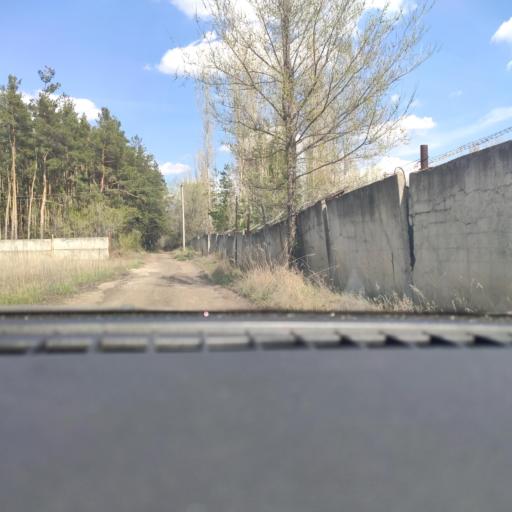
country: RU
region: Voronezj
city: Maslovka
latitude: 51.5954
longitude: 39.2165
